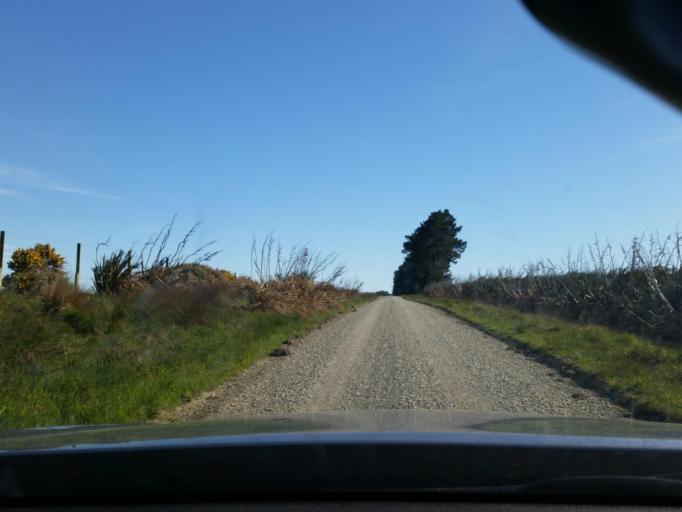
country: NZ
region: Southland
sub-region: Southland District
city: Winton
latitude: -46.2087
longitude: 168.4861
